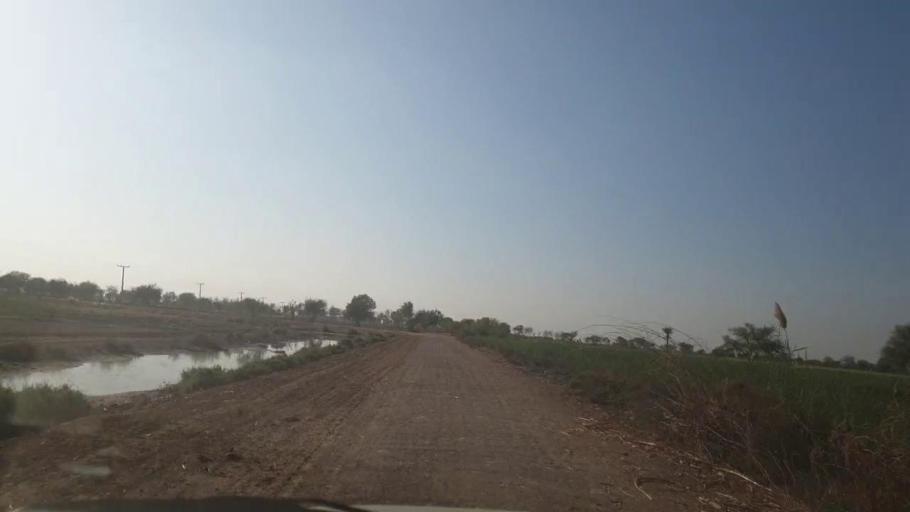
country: PK
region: Sindh
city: Mirwah Gorchani
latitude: 25.4305
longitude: 69.1242
